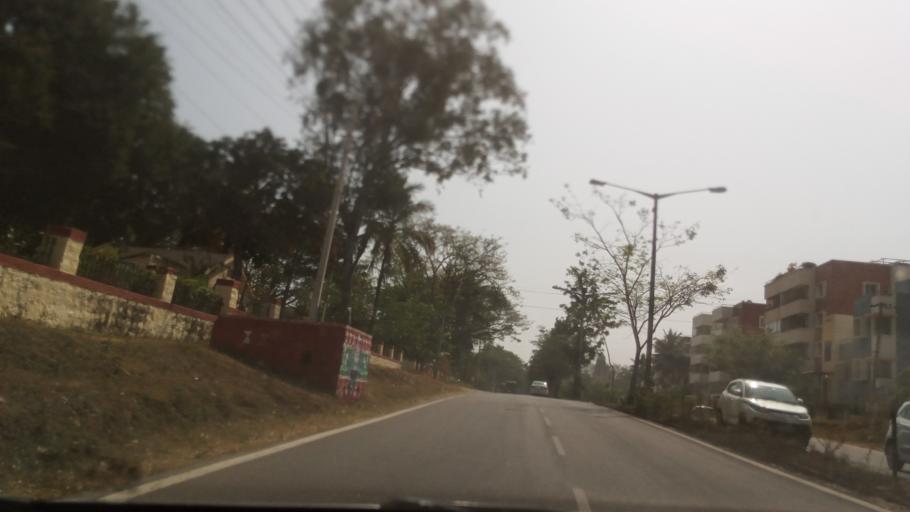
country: IN
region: Karnataka
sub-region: Mysore
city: Mysore
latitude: 12.3291
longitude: 76.6331
